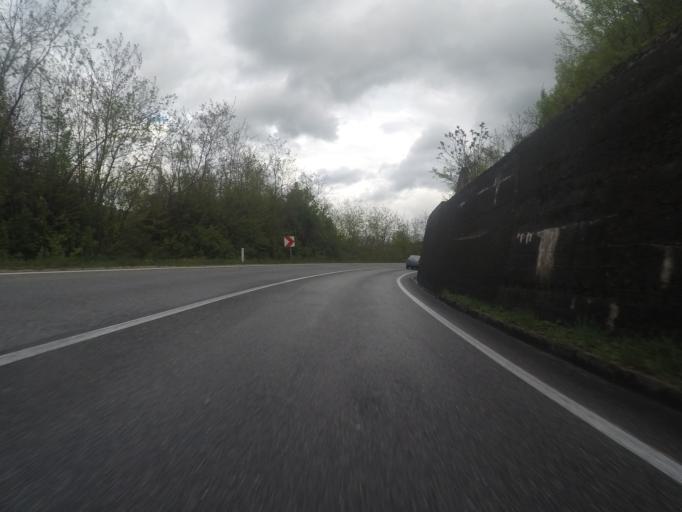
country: BA
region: Federation of Bosnia and Herzegovina
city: Konjic
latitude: 43.6908
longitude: 17.8710
